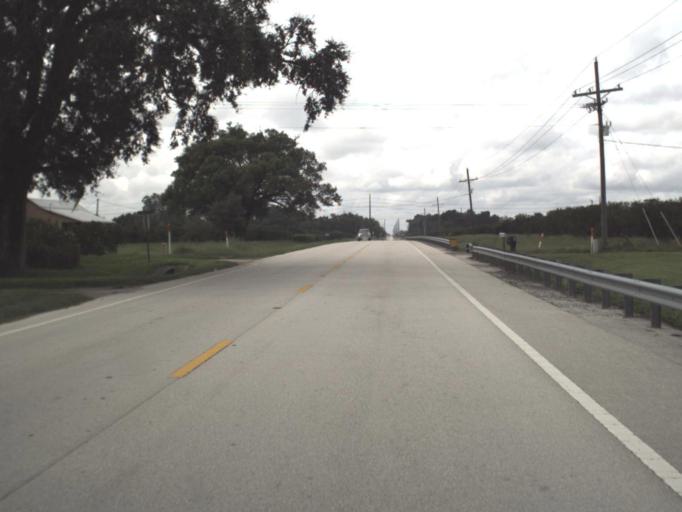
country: US
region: Florida
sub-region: Hardee County
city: Bowling Green
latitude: 27.5949
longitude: -81.9319
